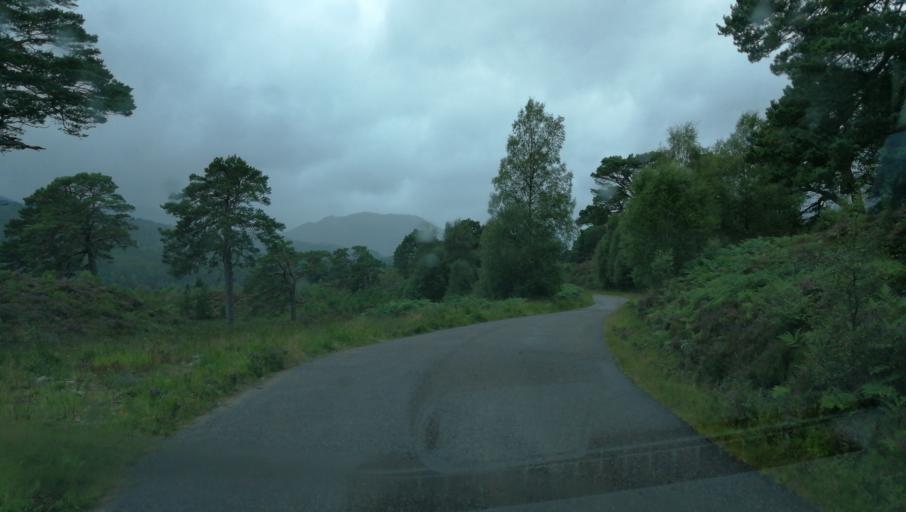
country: GB
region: Scotland
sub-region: Highland
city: Spean Bridge
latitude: 57.2683
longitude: -4.9708
